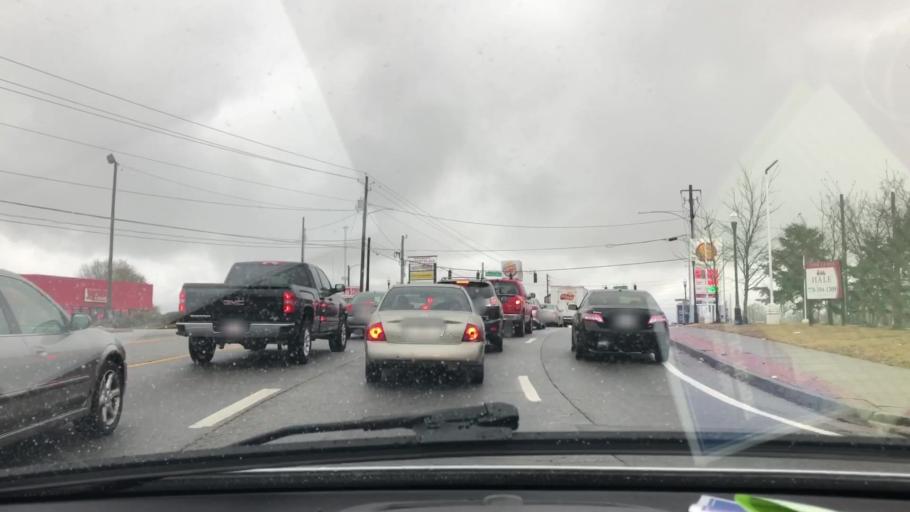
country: US
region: Georgia
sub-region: DeKalb County
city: Panthersville
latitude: 33.7124
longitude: -84.2718
